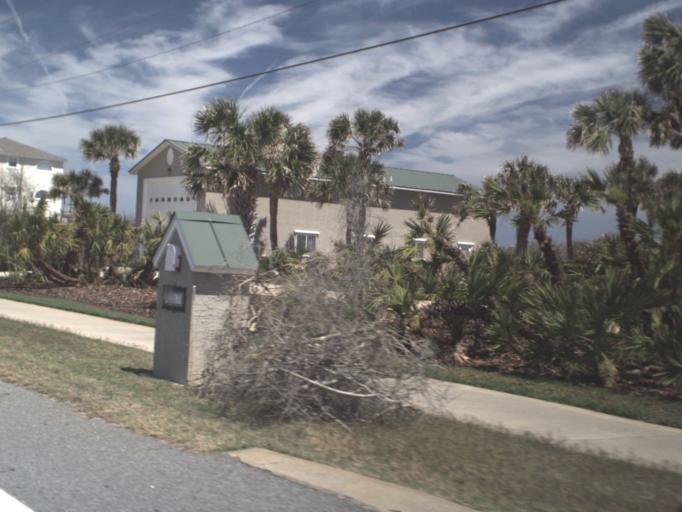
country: US
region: Florida
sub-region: Flagler County
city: Palm Coast
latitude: 29.6542
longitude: -81.2071
